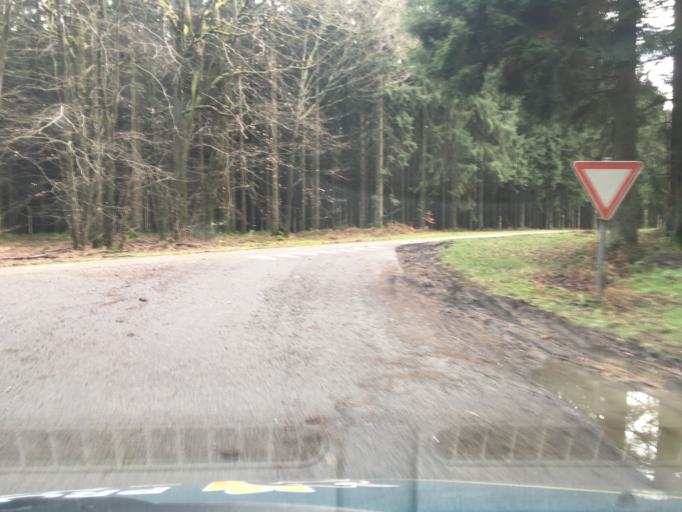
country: FR
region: Champagne-Ardenne
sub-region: Departement des Ardennes
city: Haybes
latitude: 50.0434
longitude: 4.6731
